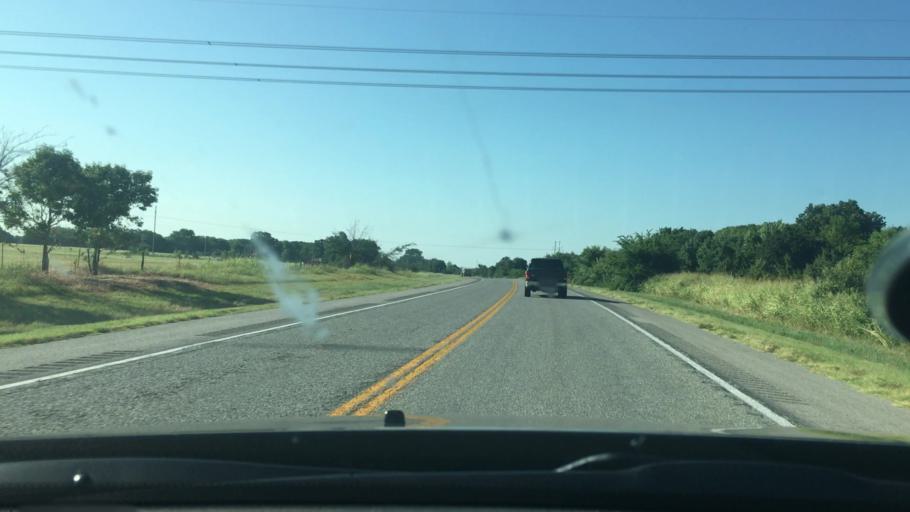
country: US
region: Oklahoma
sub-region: Johnston County
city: Tishomingo
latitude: 34.2643
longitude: -96.7717
